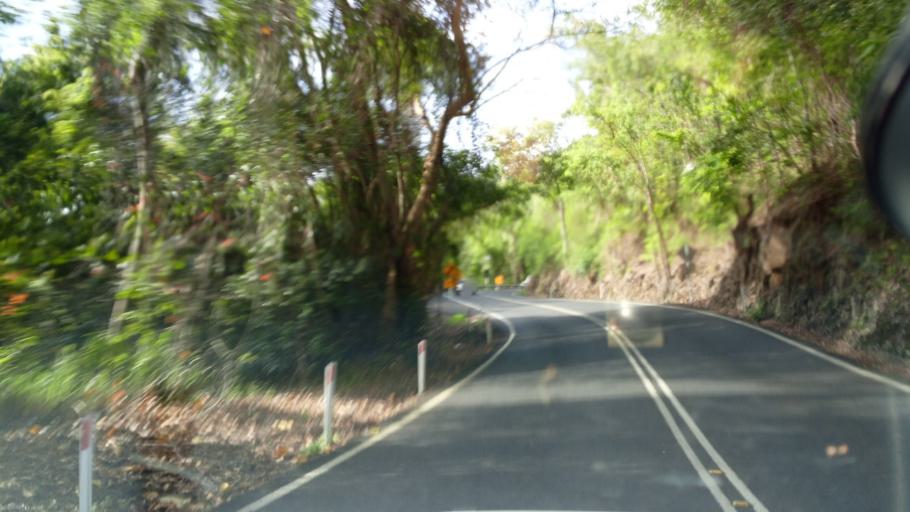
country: AU
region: Queensland
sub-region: Cairns
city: Redlynch
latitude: -16.8398
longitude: 145.6833
